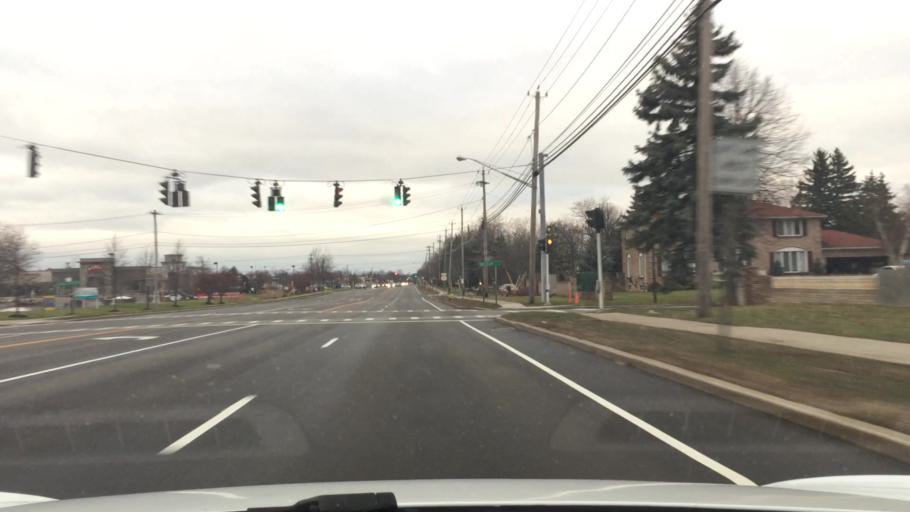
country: US
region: New York
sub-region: Erie County
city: Williamsville
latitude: 42.9786
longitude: -78.7312
